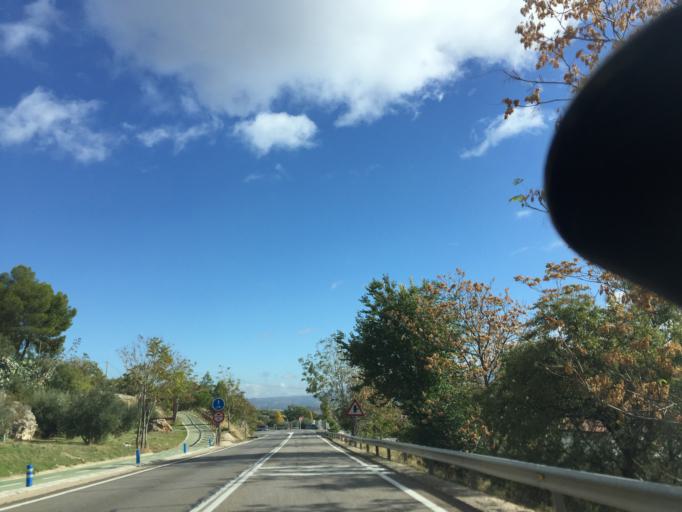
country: ES
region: Andalusia
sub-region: Provincia de Jaen
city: Jaen
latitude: 37.7522
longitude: -3.7986
